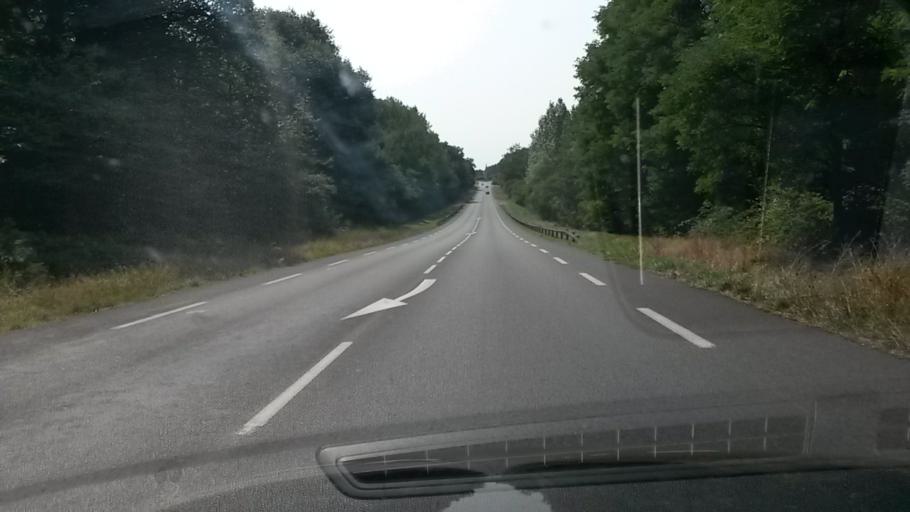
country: FR
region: Pays de la Loire
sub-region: Departement de la Mayenne
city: Chemaze
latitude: 47.7986
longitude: -0.7554
